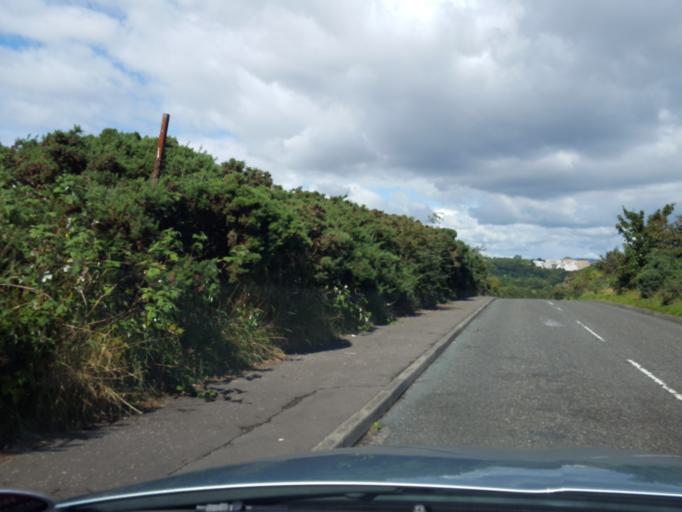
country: GB
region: Scotland
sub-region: Fife
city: North Queensferry
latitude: 56.0180
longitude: -3.4000
